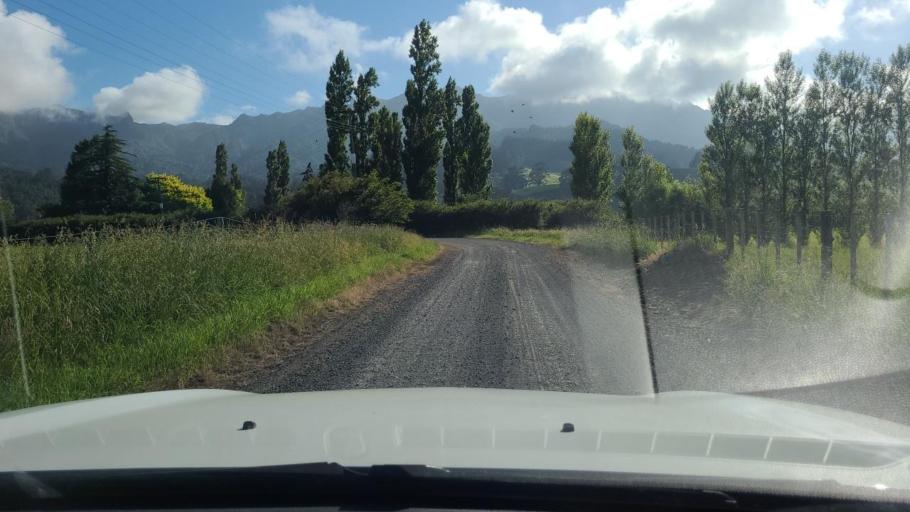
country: NZ
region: Bay of Plenty
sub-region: Western Bay of Plenty District
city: Katikati
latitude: -37.5756
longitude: 175.7613
